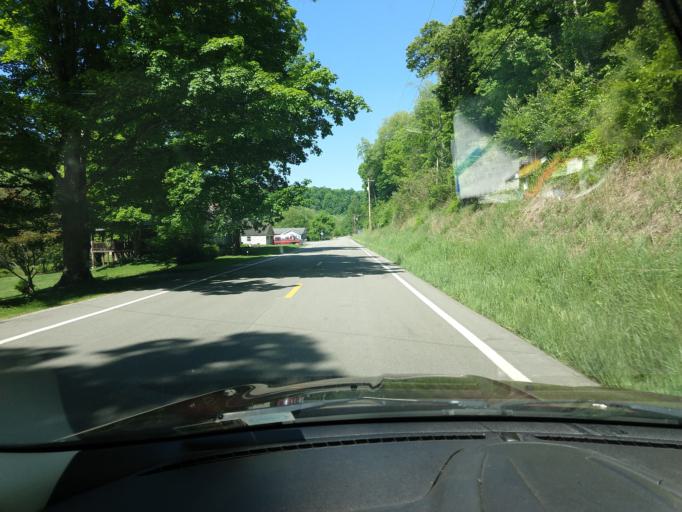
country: US
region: West Virginia
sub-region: Gilmer County
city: Glenville
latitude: 38.9156
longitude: -80.7649
